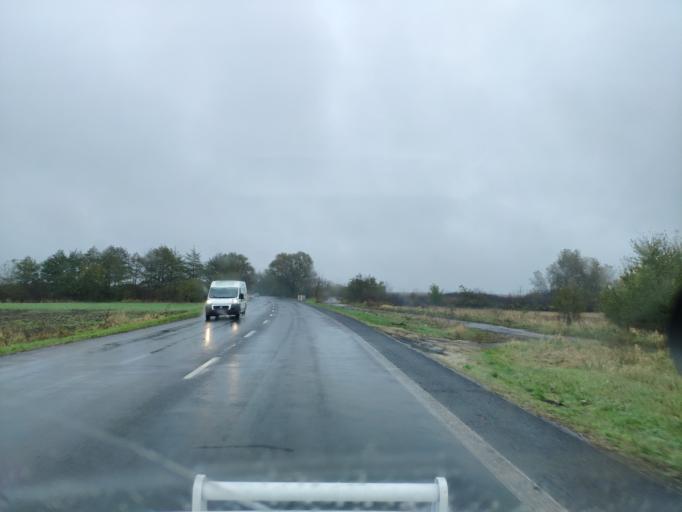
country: SK
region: Kosicky
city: Cierna nad Tisou
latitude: 48.4272
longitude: 21.9937
